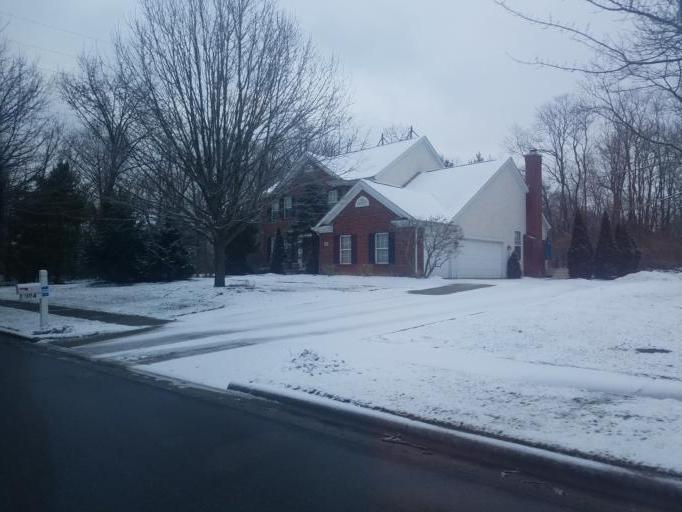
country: US
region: Ohio
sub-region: Franklin County
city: New Albany
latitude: 40.0471
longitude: -82.8314
